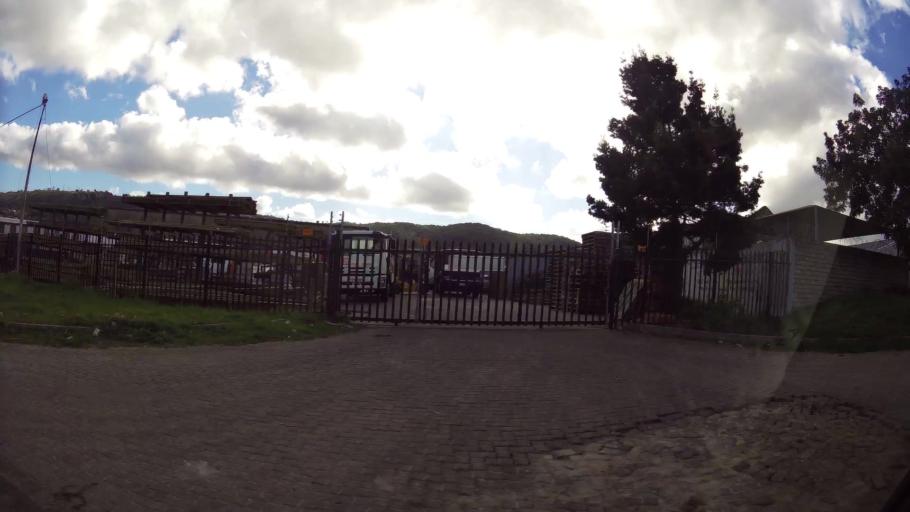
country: ZA
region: Western Cape
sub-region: Eden District Municipality
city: Knysna
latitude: -34.0458
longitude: 23.0787
